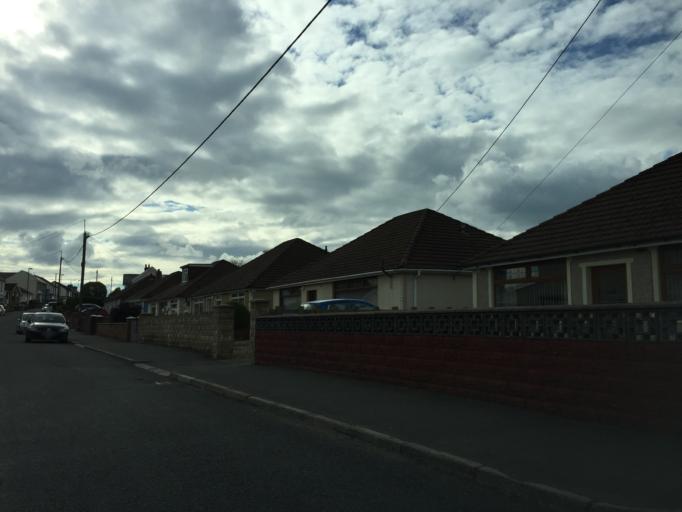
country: GB
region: Wales
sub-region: Caerphilly County Borough
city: Nelson
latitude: 51.6513
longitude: -3.2886
